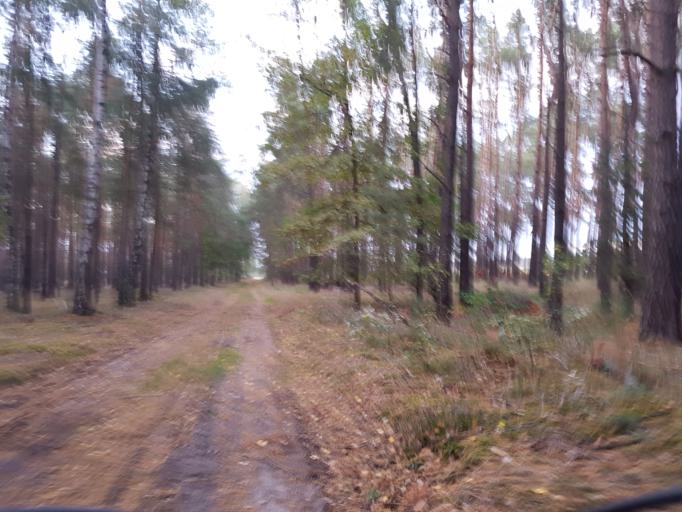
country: DE
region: Brandenburg
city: Schilda
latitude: 51.6048
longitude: 13.3642
